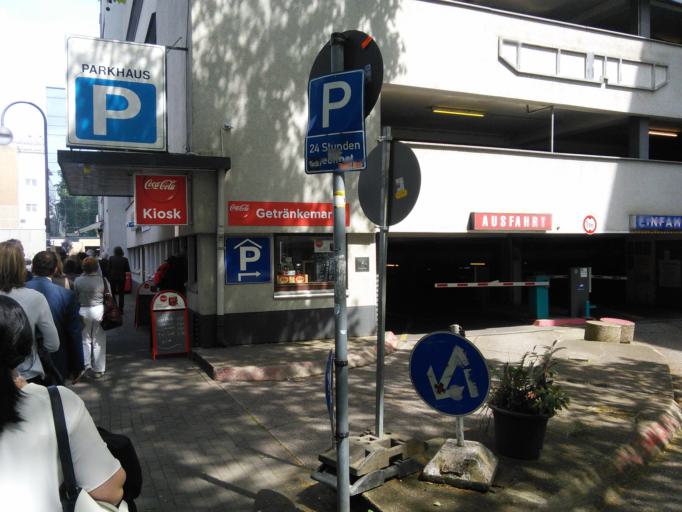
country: DE
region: North Rhine-Westphalia
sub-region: Regierungsbezirk Koln
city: Altstadt Nord
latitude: 50.9387
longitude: 6.9569
